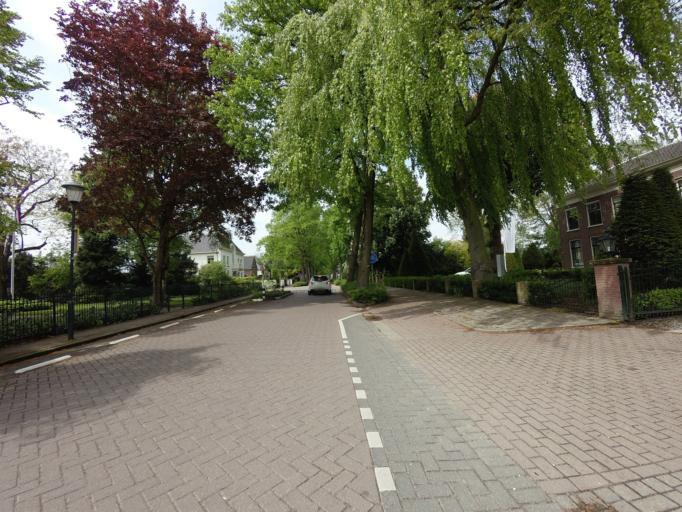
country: NL
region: South Holland
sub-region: Gemeente Binnenmaas
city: Mijnsheerenland
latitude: 51.7979
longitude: 4.4908
